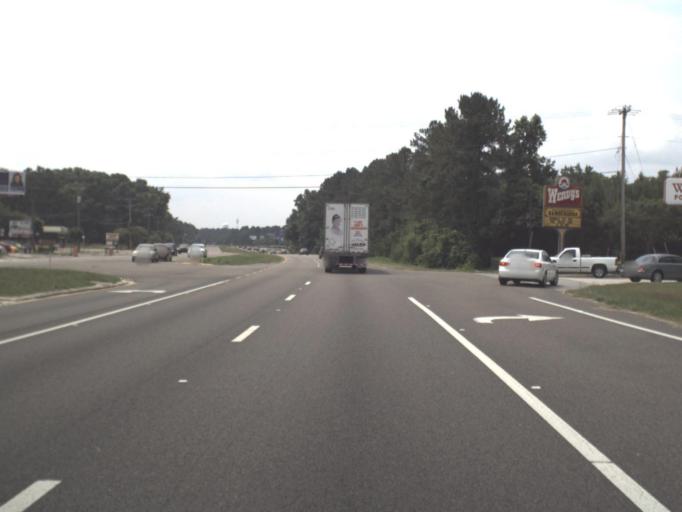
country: US
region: Florida
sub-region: Clay County
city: Green Cove Springs
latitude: 30.0226
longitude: -81.7059
